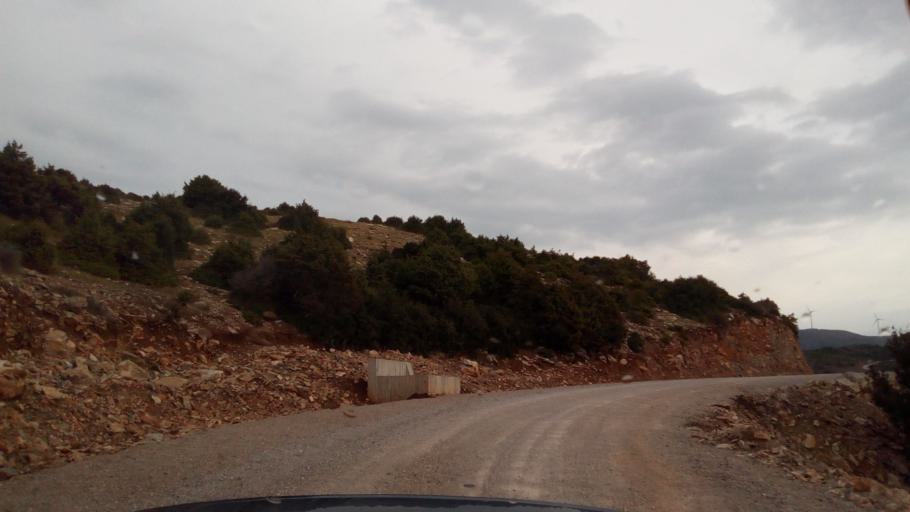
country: GR
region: West Greece
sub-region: Nomos Achaias
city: Kamarai
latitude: 38.4293
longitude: 22.0494
